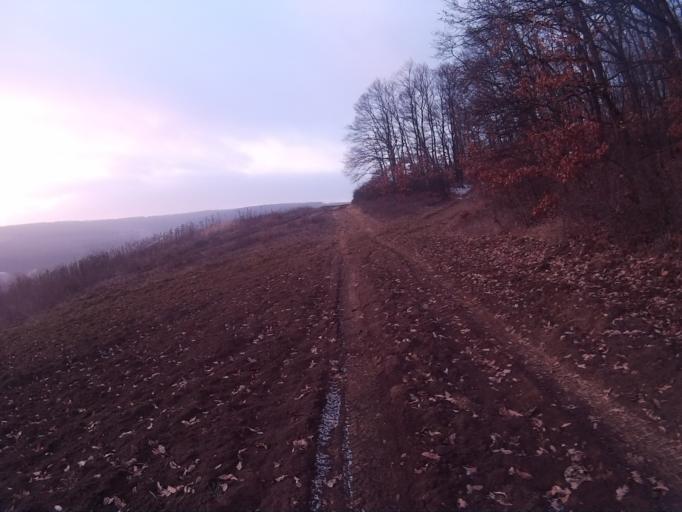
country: HU
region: Borsod-Abauj-Zemplen
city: Szendro
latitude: 48.4116
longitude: 20.8740
